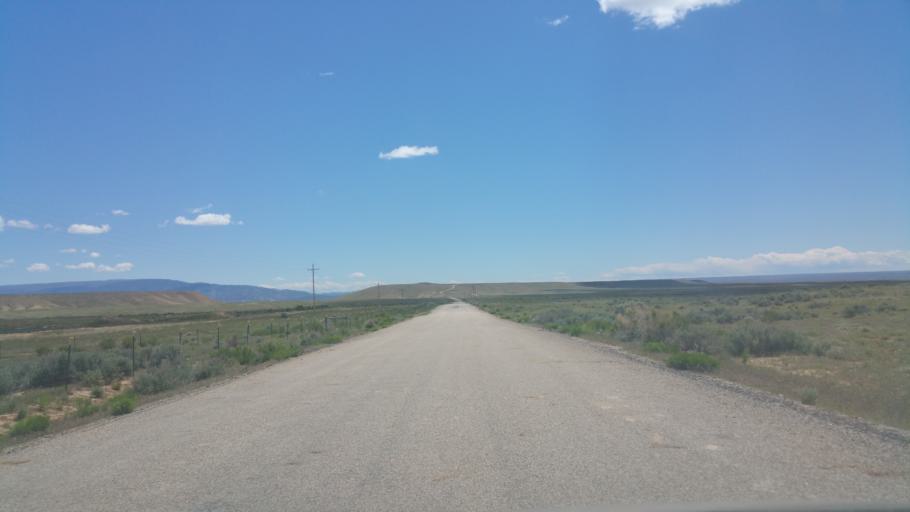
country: US
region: Utah
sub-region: Uintah County
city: Naples
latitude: 40.4646
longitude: -109.4461
